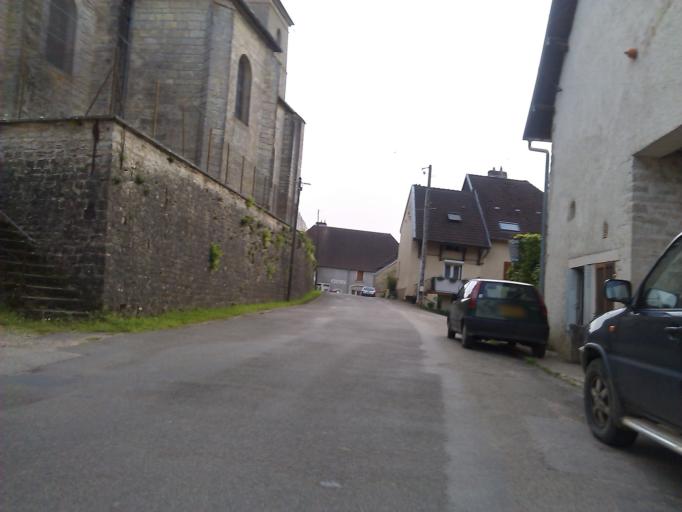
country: FR
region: Franche-Comte
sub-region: Departement du Jura
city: Orchamps
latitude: 47.1312
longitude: 5.6915
